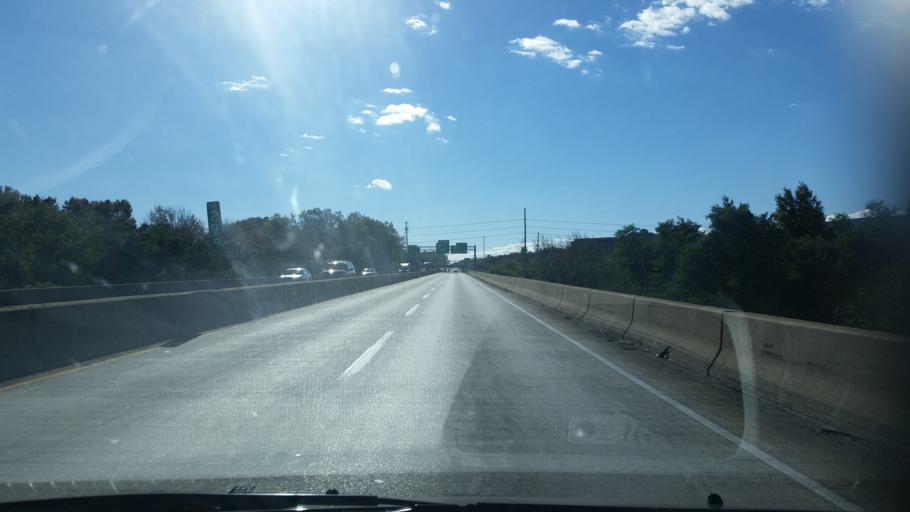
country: US
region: Pennsylvania
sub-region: Berks County
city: Hamburg
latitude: 40.5594
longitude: -75.9920
